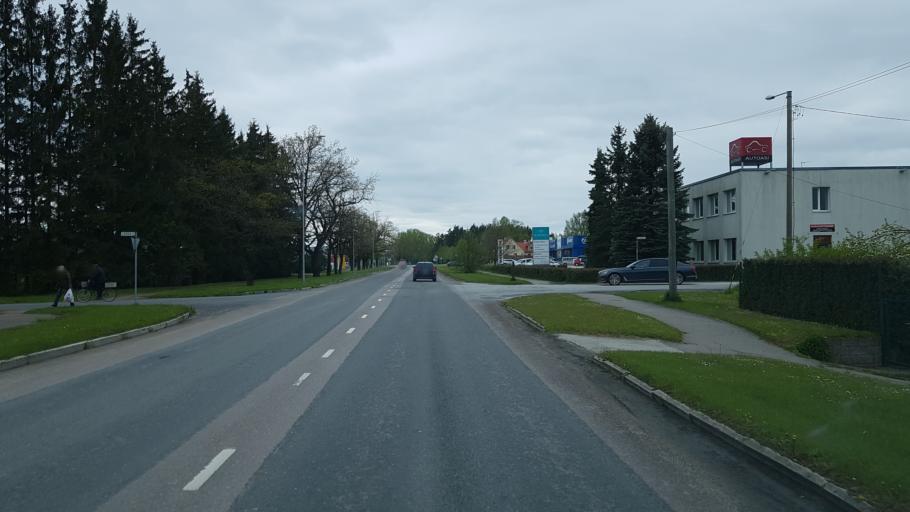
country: EE
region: Viljandimaa
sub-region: Viljandi linn
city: Viljandi
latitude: 58.3751
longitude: 25.5984
